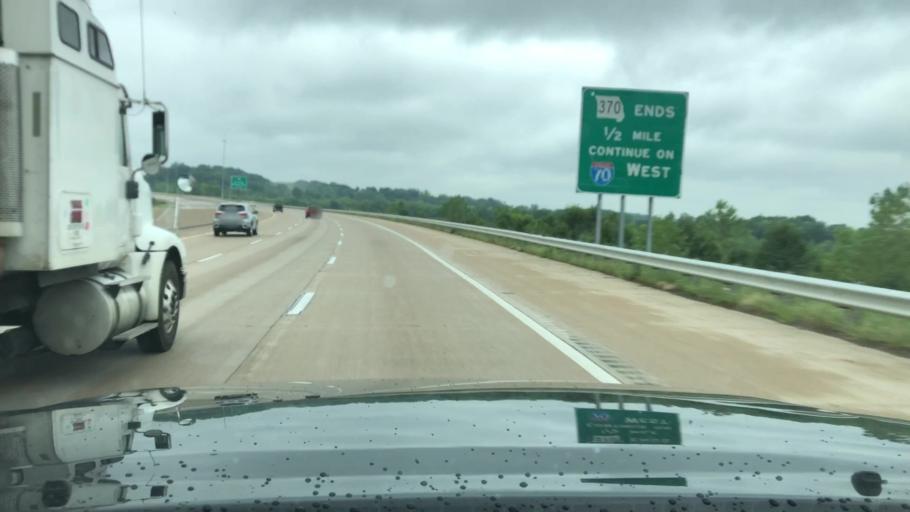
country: US
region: Missouri
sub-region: Saint Charles County
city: Saint Peters
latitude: 38.8107
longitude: -90.5869
